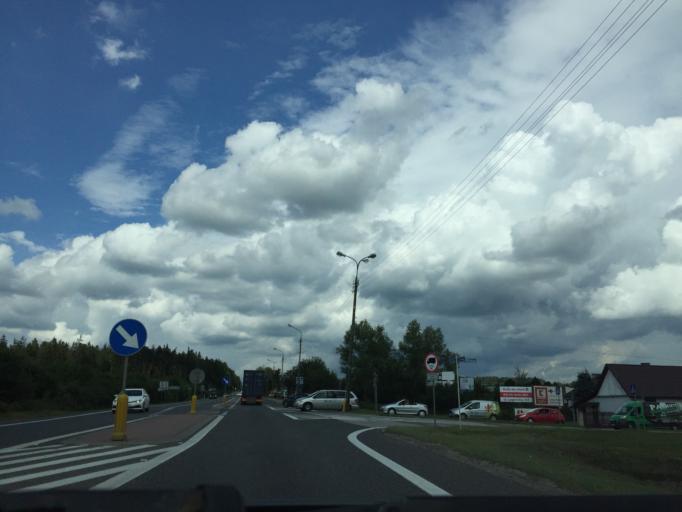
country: PL
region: Swietokrzyskie
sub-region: Powiat skarzyski
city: Skarzysko-Kamienna
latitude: 51.1182
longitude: 20.8498
